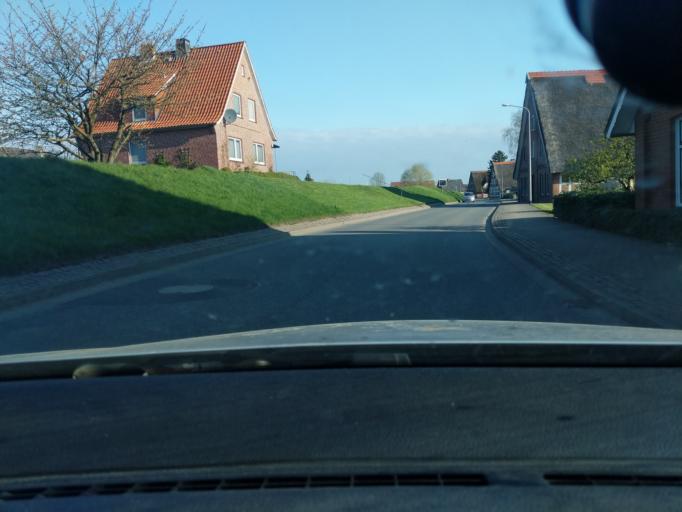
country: DE
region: Lower Saxony
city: Guderhandviertel
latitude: 53.5474
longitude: 9.6108
